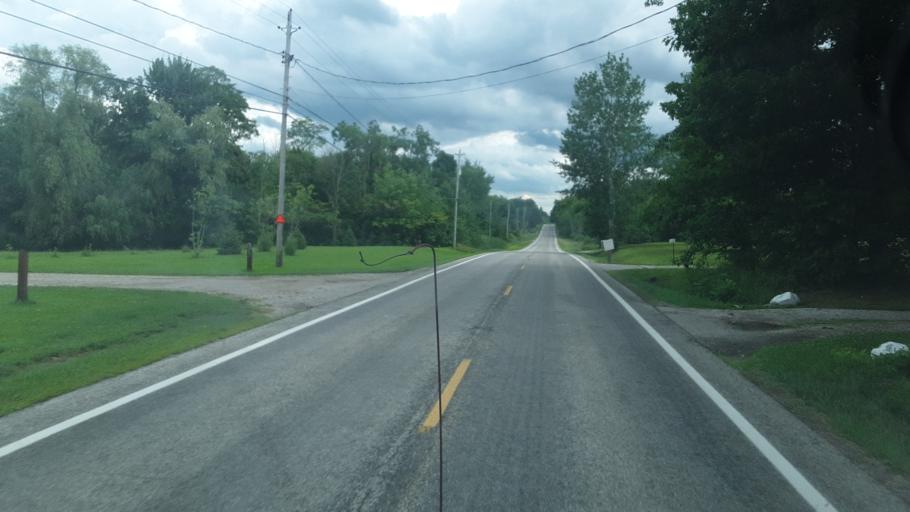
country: US
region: Ohio
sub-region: Ashtabula County
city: Jefferson
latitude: 41.7101
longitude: -80.7812
